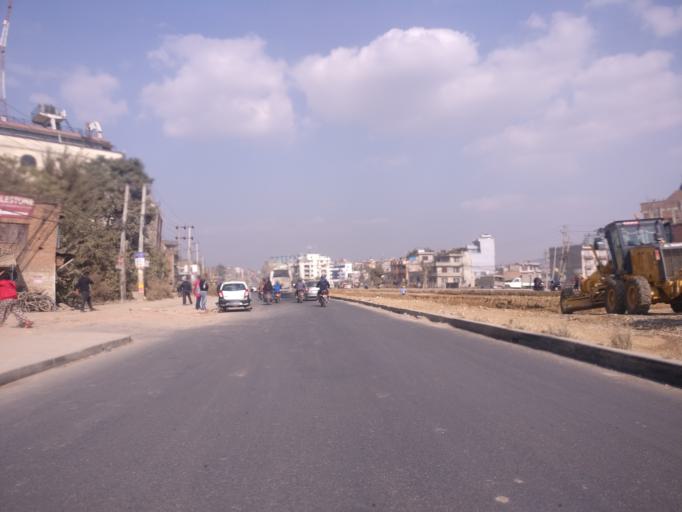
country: NP
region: Central Region
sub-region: Bagmati Zone
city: Patan
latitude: 27.6714
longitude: 85.3399
